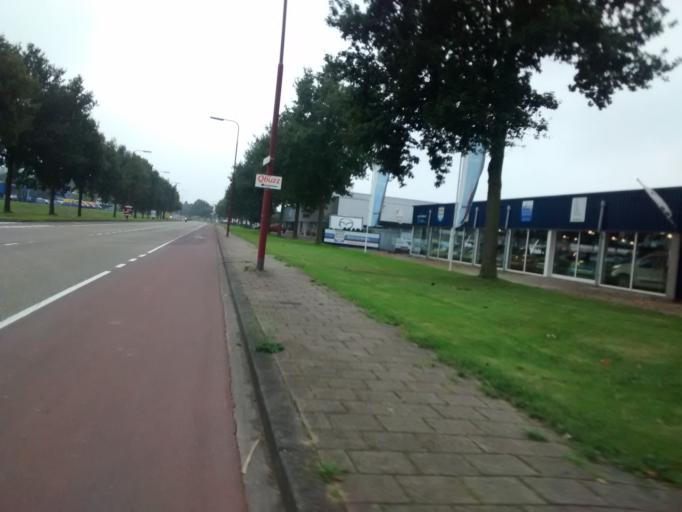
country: NL
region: Utrecht
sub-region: Gemeente Nieuwegein
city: Nieuwegein
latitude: 52.0302
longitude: 5.1052
